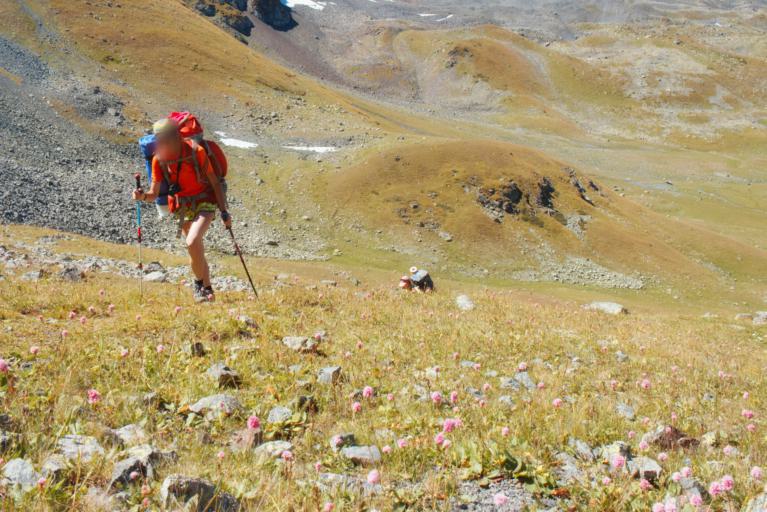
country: RU
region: Karachayevo-Cherkesiya
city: Nizhniy Arkhyz
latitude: 43.6030
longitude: 41.1668
